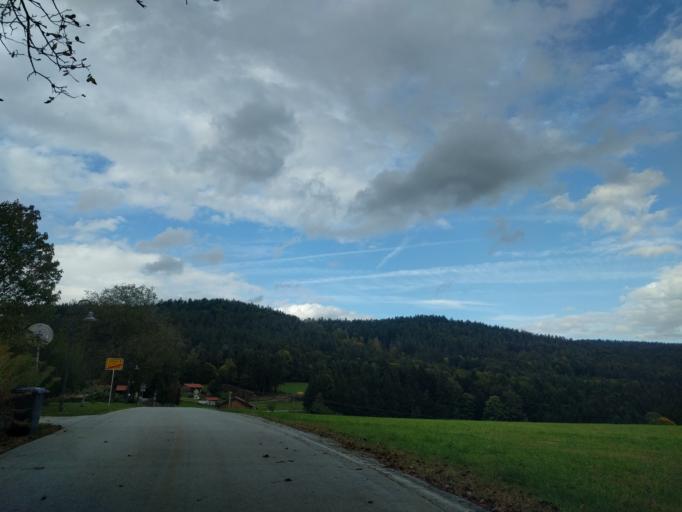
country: DE
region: Bavaria
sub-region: Lower Bavaria
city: Schaufling
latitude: 48.8718
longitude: 13.0286
